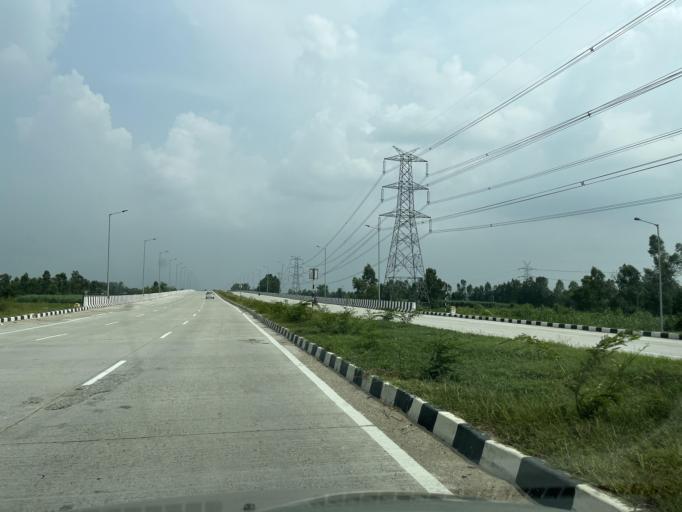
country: IN
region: Uttarakhand
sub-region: Udham Singh Nagar
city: Jaspur
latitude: 29.2972
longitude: 78.8382
